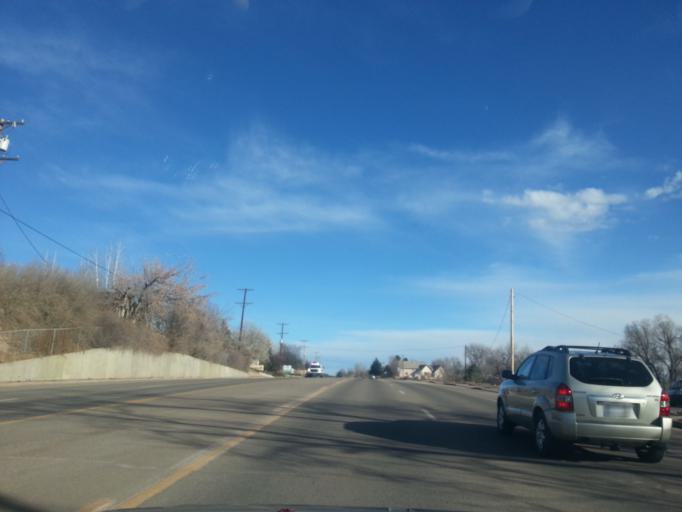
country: US
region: Colorado
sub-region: Larimer County
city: Loveland
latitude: 40.4072
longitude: -105.1276
